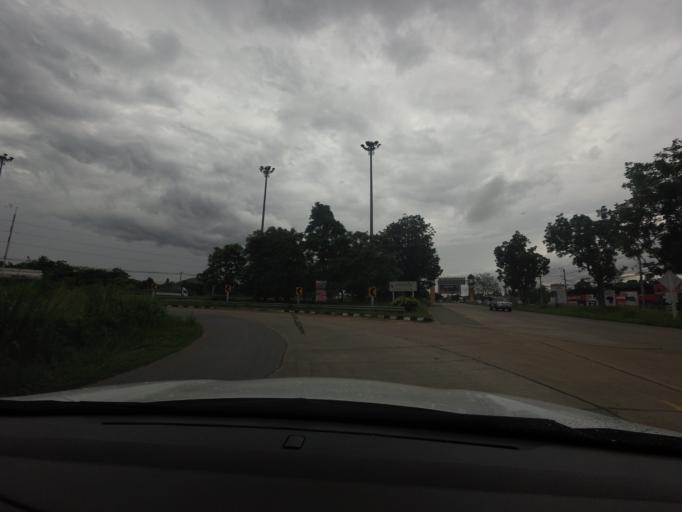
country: TH
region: Nakhon Ratchasima
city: Pak Chong
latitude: 14.6605
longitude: 101.3897
